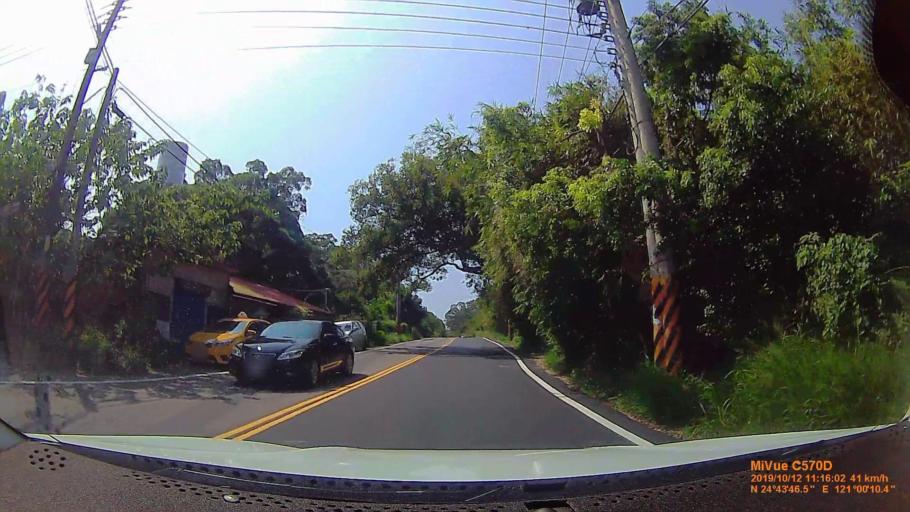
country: TW
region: Taiwan
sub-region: Hsinchu
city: Hsinchu
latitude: 24.7296
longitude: 121.0028
